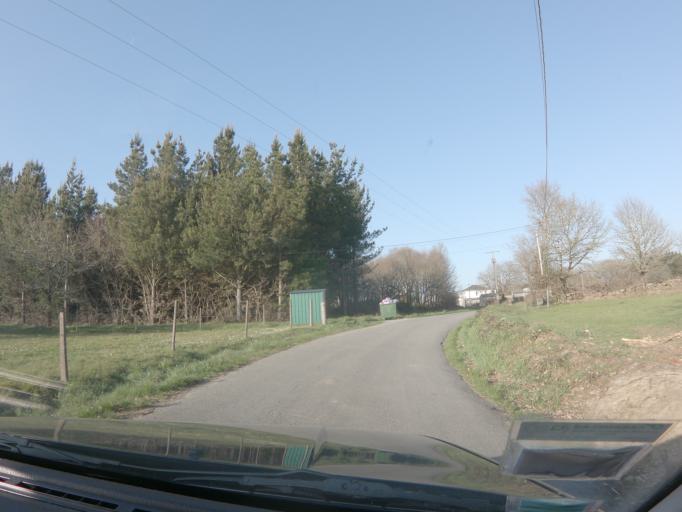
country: ES
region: Galicia
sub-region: Provincia de Lugo
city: Corgo
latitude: 42.9421
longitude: -7.4377
